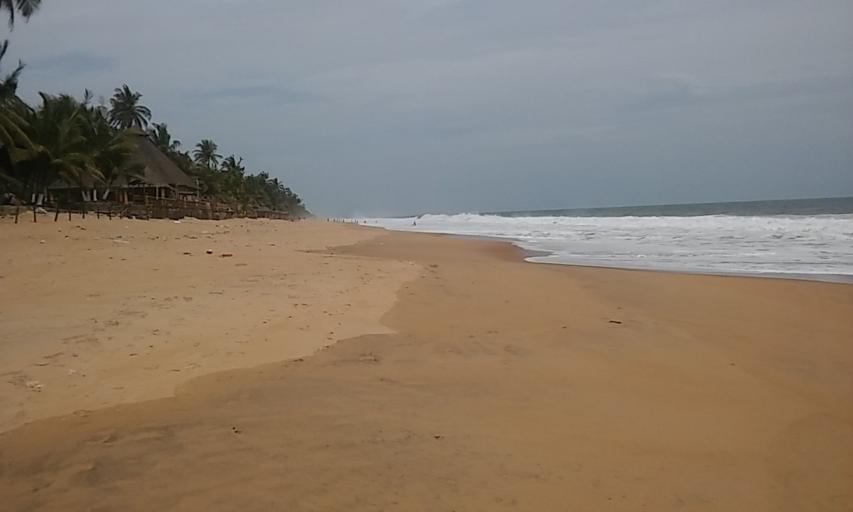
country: CI
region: Sud-Comoe
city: Grand-Bassam
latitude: 5.1963
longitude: -3.7484
